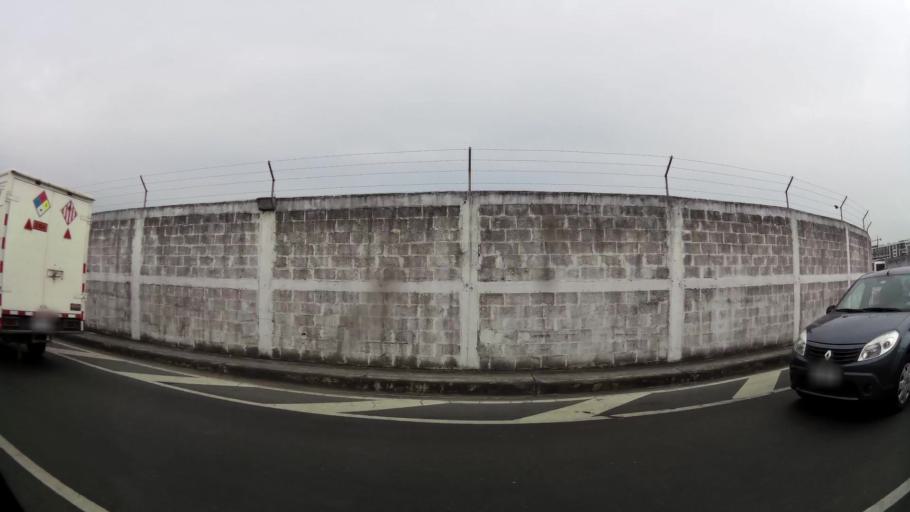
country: EC
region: Guayas
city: Eloy Alfaro
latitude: -2.1446
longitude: -79.8779
